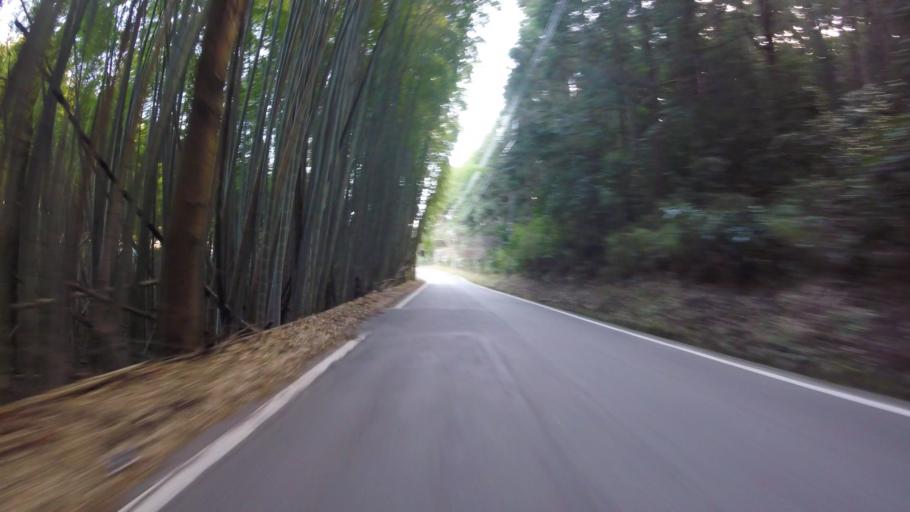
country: JP
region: Shizuoka
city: Atami
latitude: 35.1129
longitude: 139.0099
